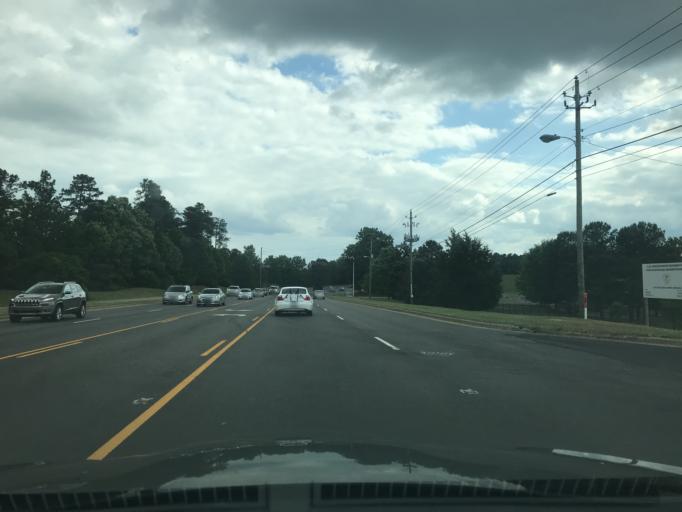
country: US
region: North Carolina
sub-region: Wake County
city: Wake Forest
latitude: 35.9152
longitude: -78.5950
